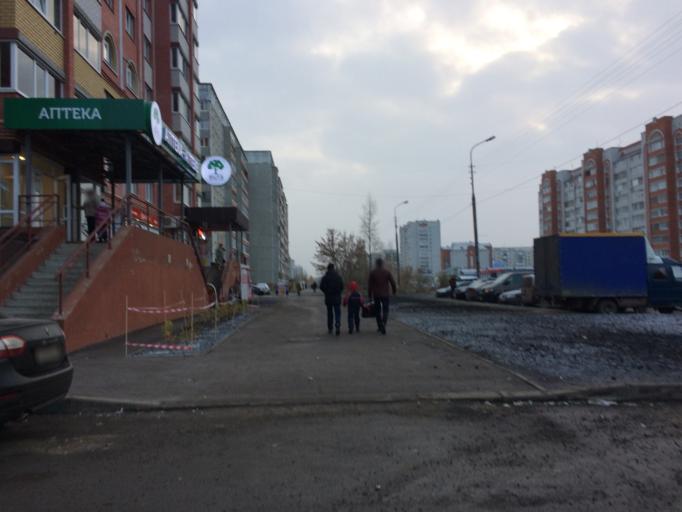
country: RU
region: Mariy-El
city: Yoshkar-Ola
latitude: 56.6387
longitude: 47.9238
